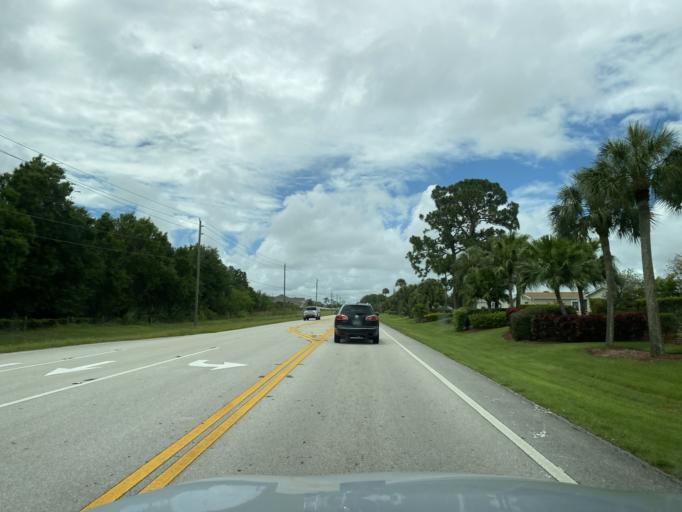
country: US
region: Florida
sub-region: Brevard County
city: West Melbourne
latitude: 28.0490
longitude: -80.6543
